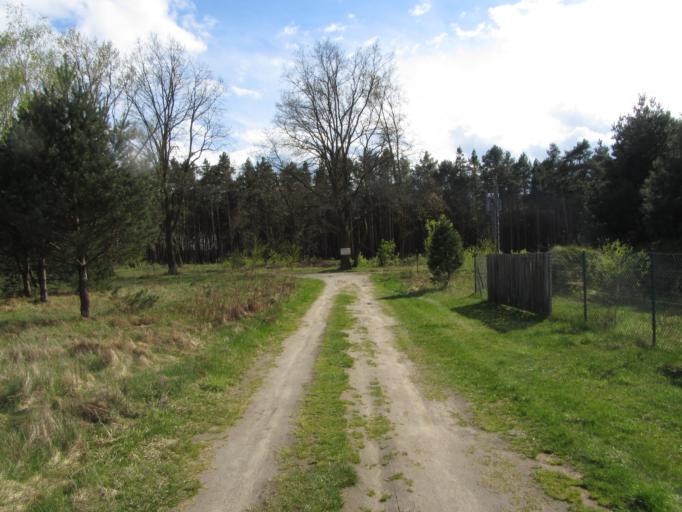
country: PL
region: Lubusz
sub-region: Powiat wschowski
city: Slawa
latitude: 51.8728
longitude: 15.9987
